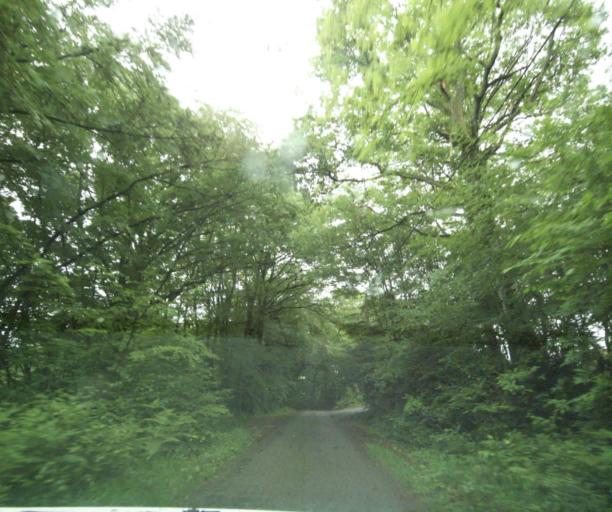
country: FR
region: Bourgogne
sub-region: Departement de Saone-et-Loire
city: Charolles
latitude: 46.5053
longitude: 4.2963
